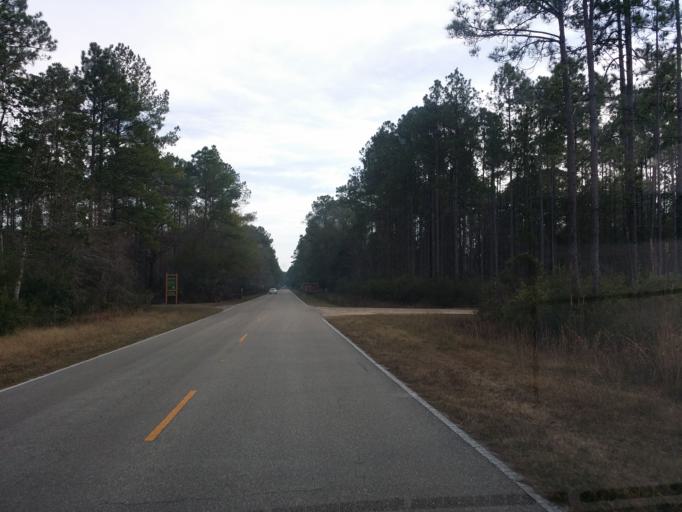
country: US
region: Florida
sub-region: Leon County
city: Woodville
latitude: 30.1611
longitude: -84.1537
